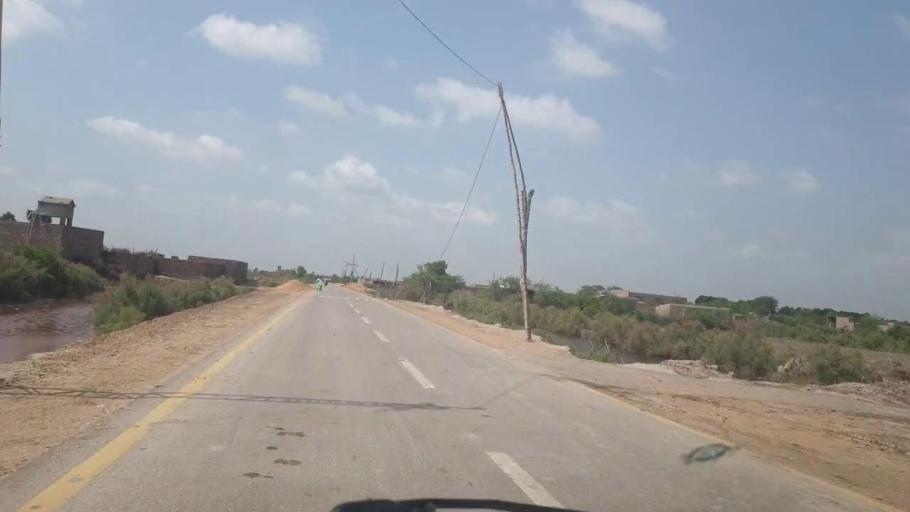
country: PK
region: Sindh
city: Berani
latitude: 25.6854
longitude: 68.9269
